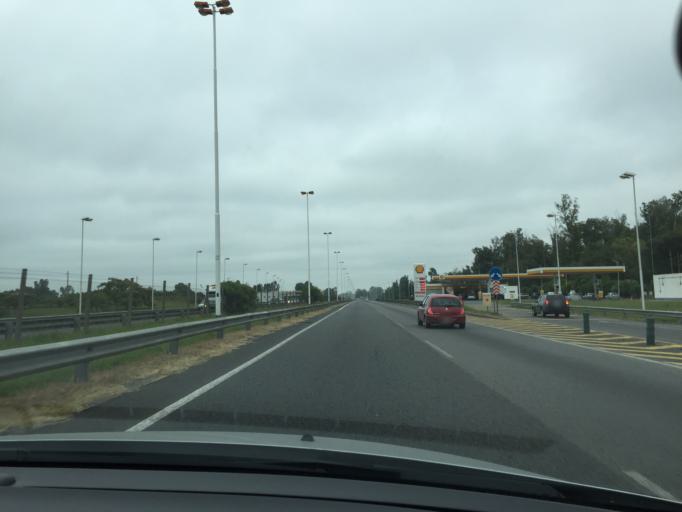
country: AR
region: Buenos Aires
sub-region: Partido de Ezeiza
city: Ezeiza
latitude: -34.8595
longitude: -58.5626
